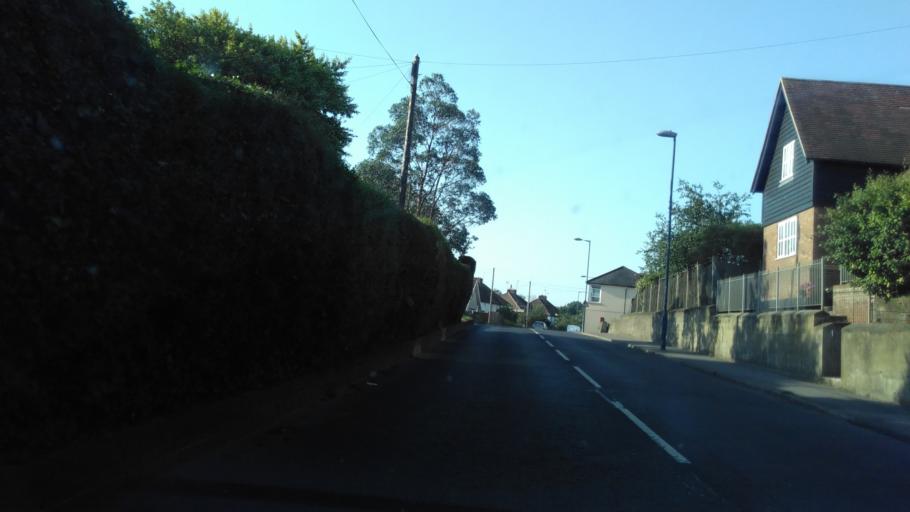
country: GB
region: England
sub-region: Kent
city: Whitstable
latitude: 51.3456
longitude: 1.0215
